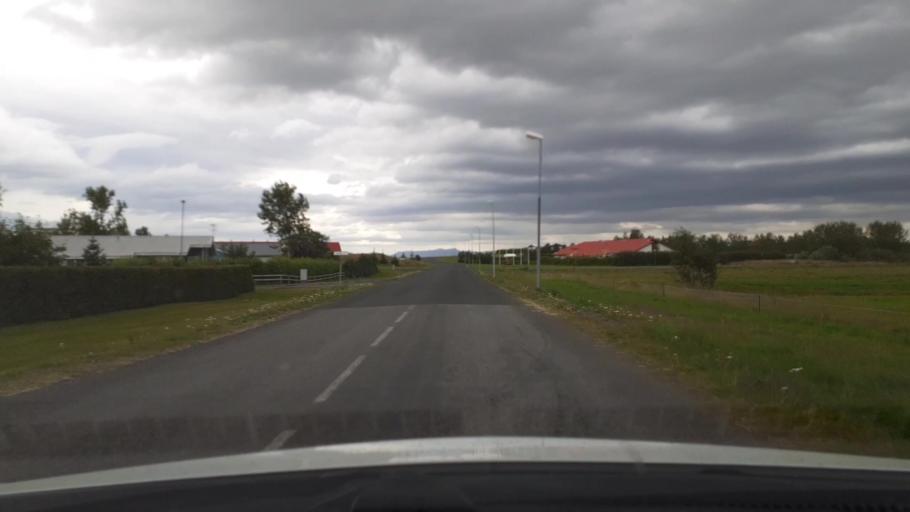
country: IS
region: West
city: Borgarnes
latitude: 64.5632
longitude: -21.7602
